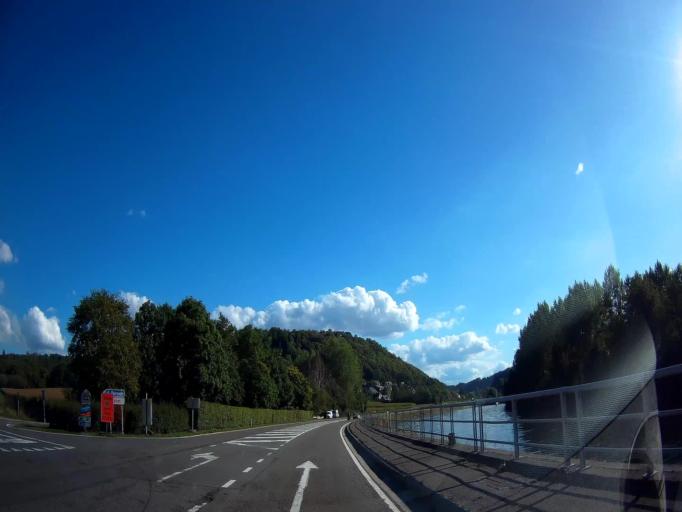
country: BE
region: Wallonia
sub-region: Province de Namur
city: Anhee
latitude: 50.2998
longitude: 4.8992
